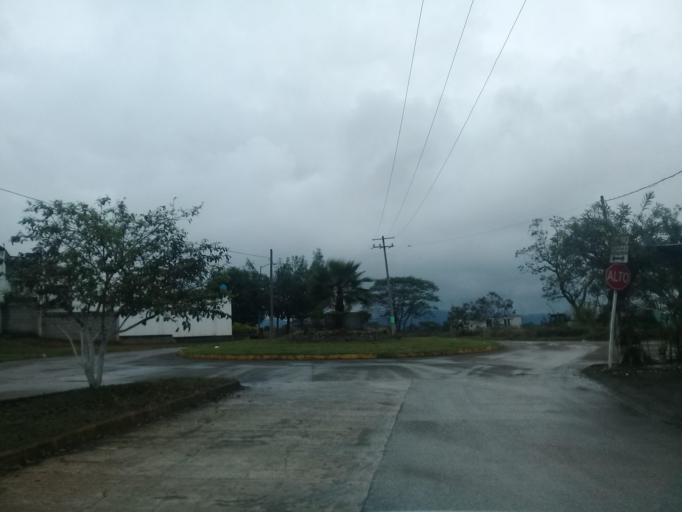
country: MX
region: Veracruz
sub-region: Amatlan de los Reyes
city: Trapiche Viejo
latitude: 18.8367
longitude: -96.9526
